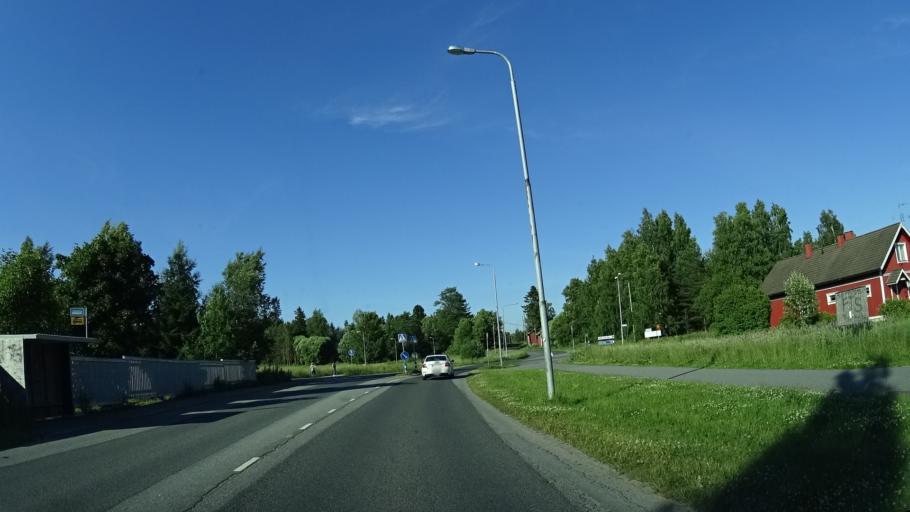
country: FI
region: Satakunta
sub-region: Pori
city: Ulvila
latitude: 61.5072
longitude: 21.8608
